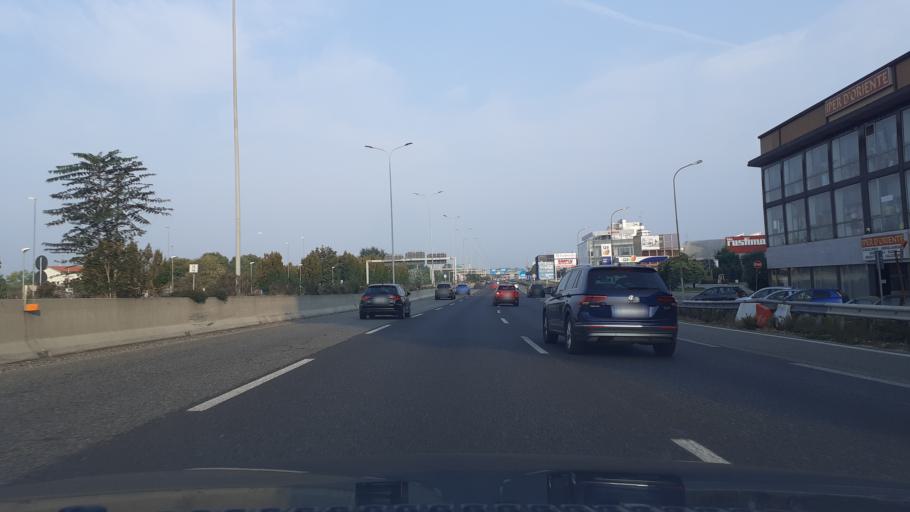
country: IT
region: Lombardy
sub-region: Provincia di Monza e Brianza
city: Muggio
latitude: 45.6011
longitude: 9.2324
